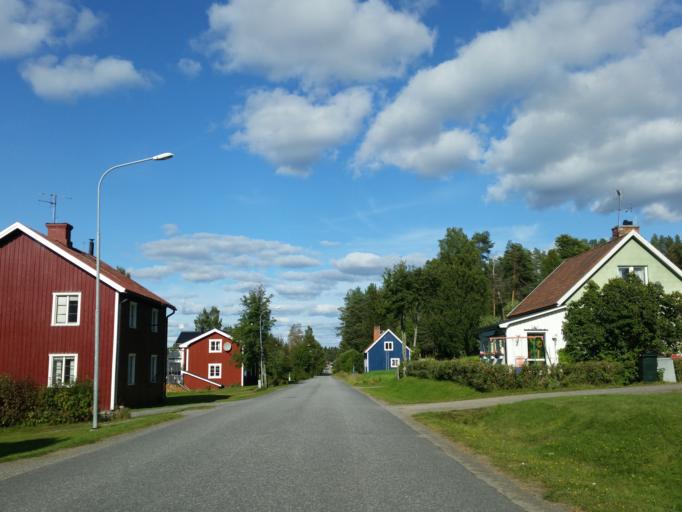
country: SE
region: Vaesterbotten
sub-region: Robertsfors Kommun
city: Robertsfors
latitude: 64.1666
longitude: 20.9320
